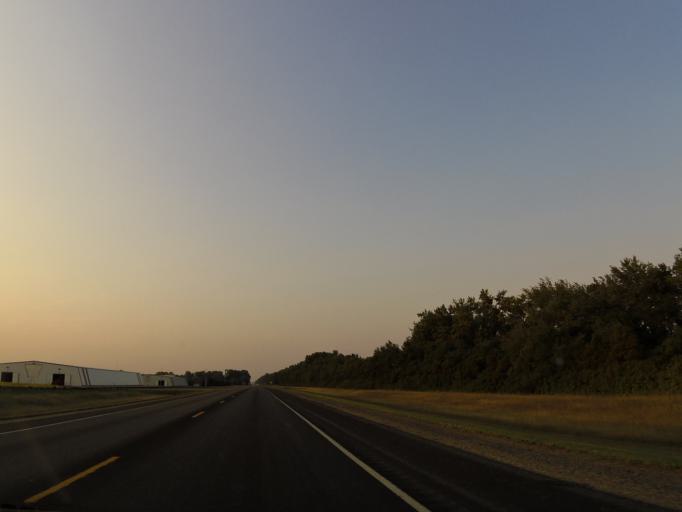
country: US
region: North Dakota
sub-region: Grand Forks County
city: Larimore
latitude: 47.9405
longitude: -97.6239
